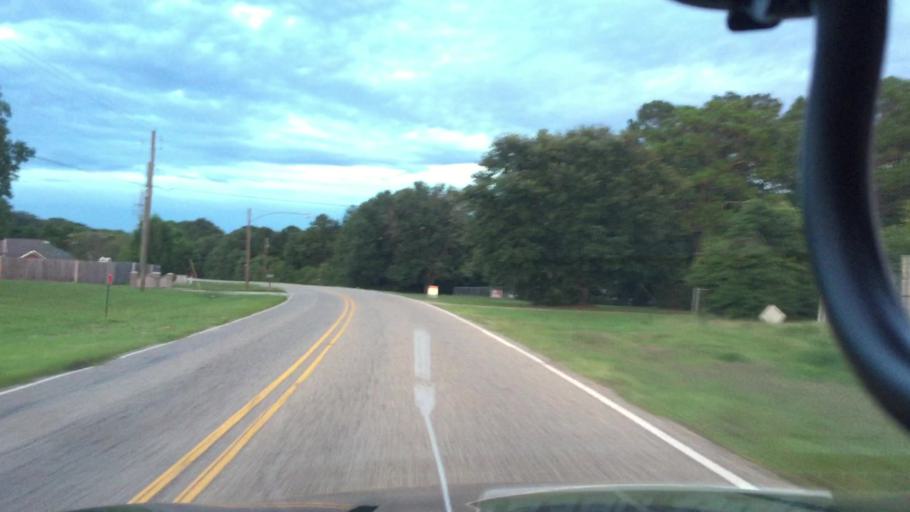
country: US
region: Alabama
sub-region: Coffee County
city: Enterprise
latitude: 31.3677
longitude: -85.8470
